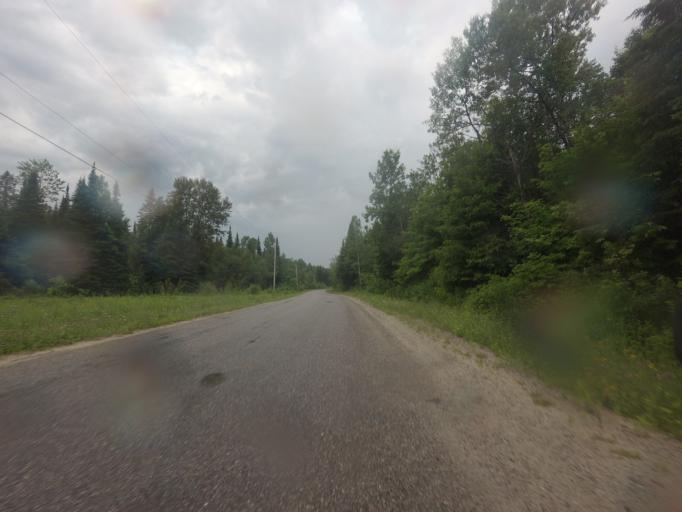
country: CA
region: Quebec
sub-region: Outaouais
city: Maniwaki
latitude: 46.4370
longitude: -75.9417
